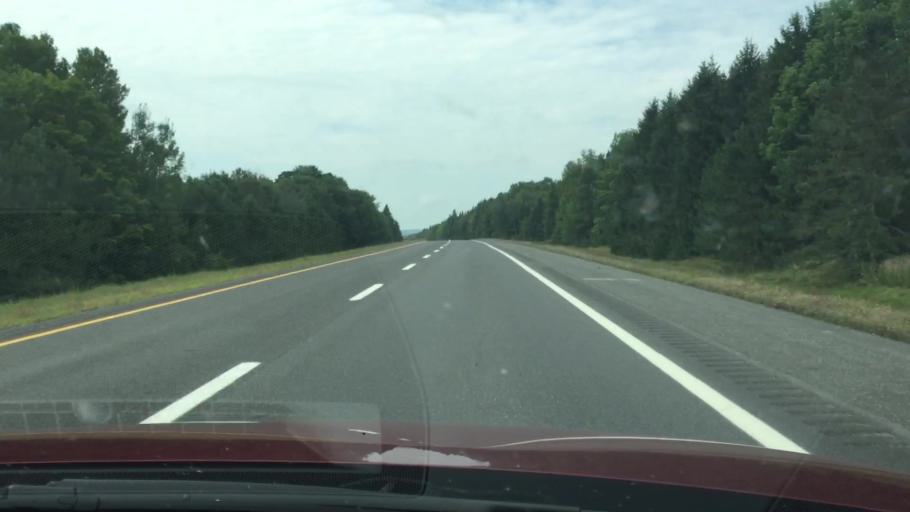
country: US
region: Maine
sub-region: Aroostook County
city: Houlton
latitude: 46.1416
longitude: -67.9399
